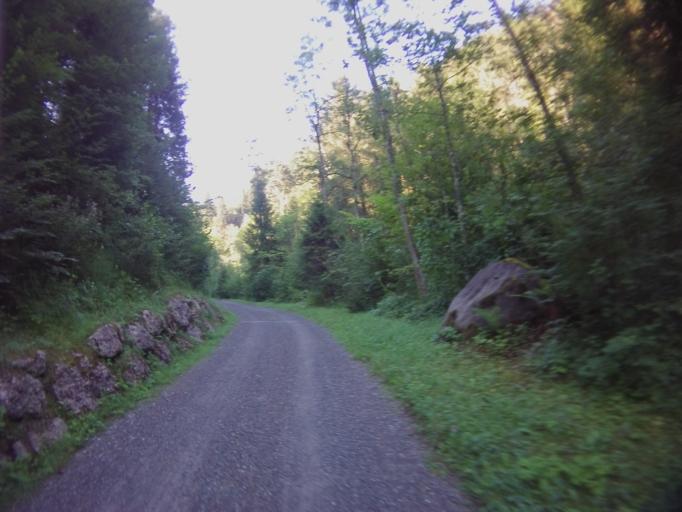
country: CH
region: Zug
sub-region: Zug
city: Menzingen
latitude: 47.1676
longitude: 8.5592
